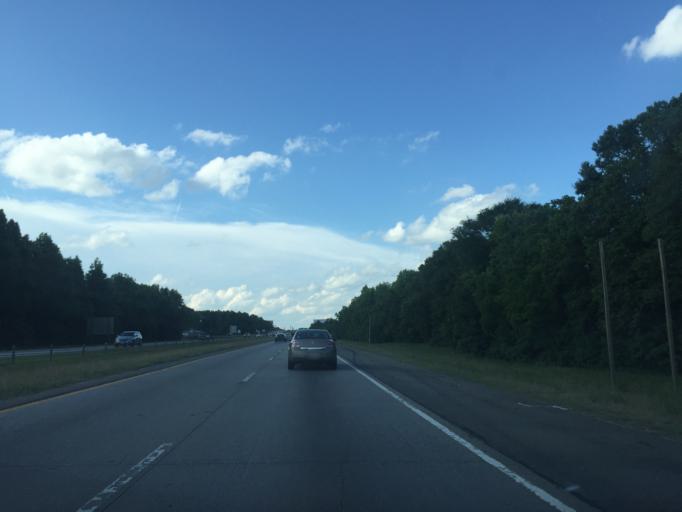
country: US
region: Georgia
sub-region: Chatham County
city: Savannah
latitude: 32.0600
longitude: -81.1393
